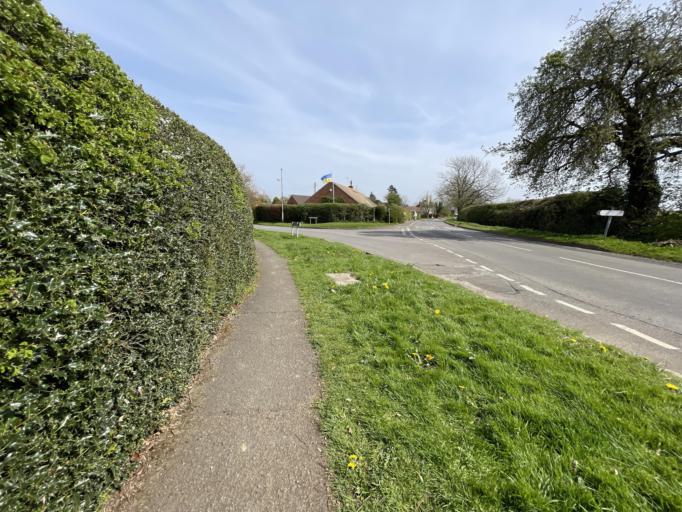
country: GB
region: England
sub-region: Leicestershire
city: Market Harborough
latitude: 52.4375
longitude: -1.0046
